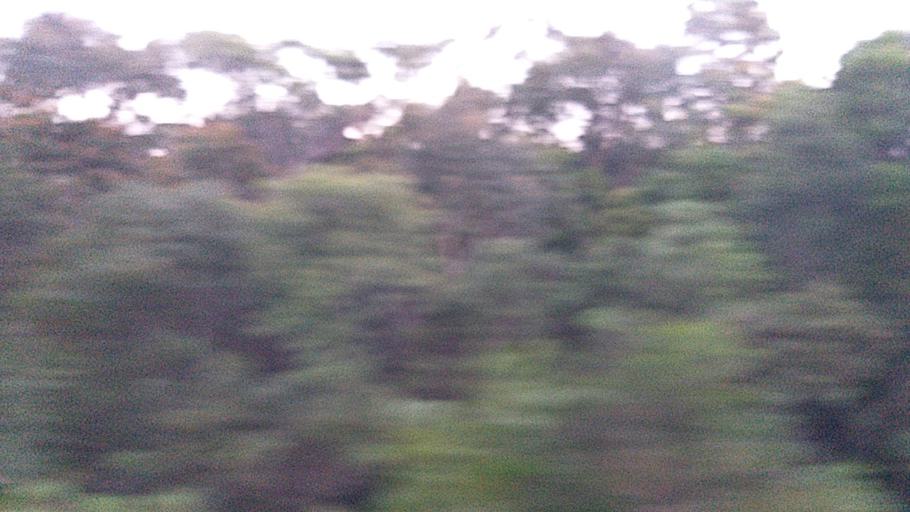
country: AU
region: New South Wales
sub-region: Wollongong
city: Helensburgh
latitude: -34.1628
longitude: 151.0012
